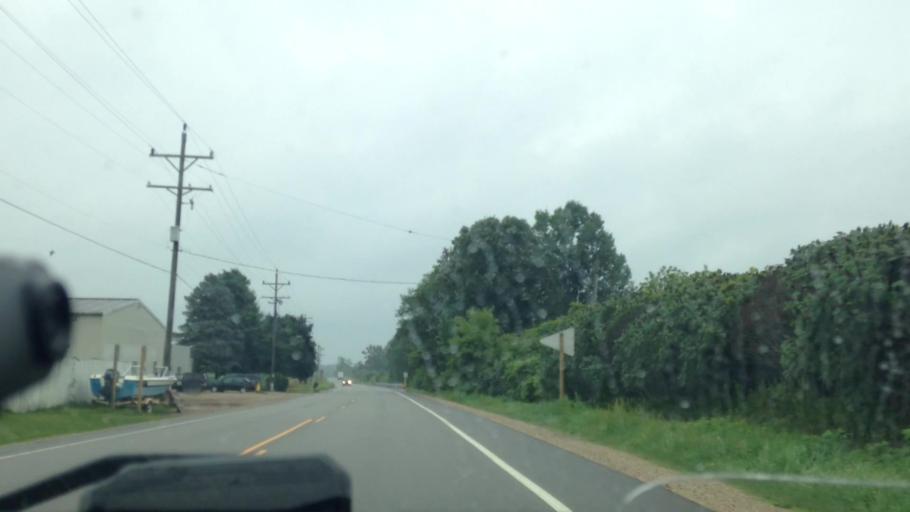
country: US
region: Wisconsin
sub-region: Washington County
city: Slinger
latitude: 43.3091
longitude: -88.2562
